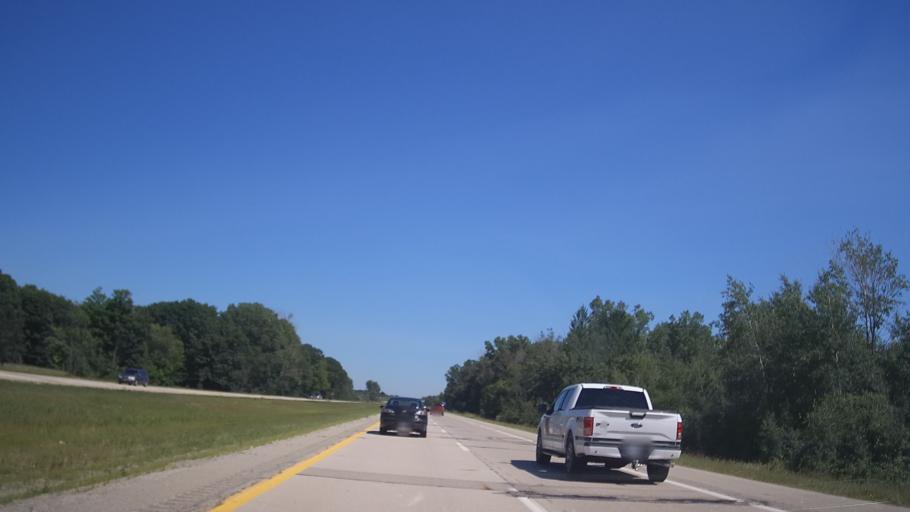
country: US
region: Michigan
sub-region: Clare County
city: Clare
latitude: 43.8056
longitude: -84.6833
